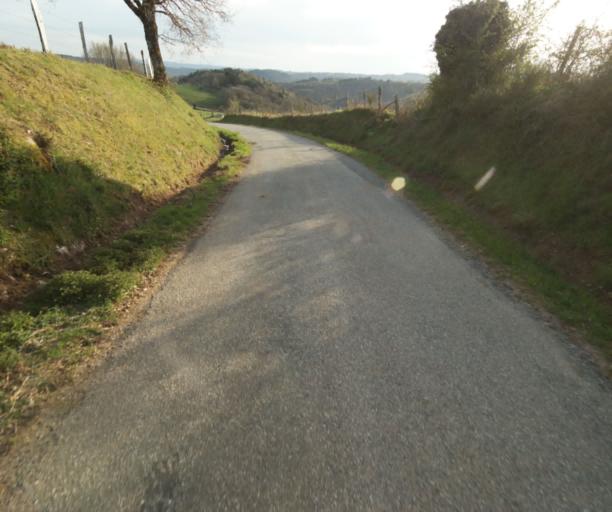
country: FR
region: Limousin
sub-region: Departement de la Correze
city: Correze
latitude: 45.3708
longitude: 1.8334
